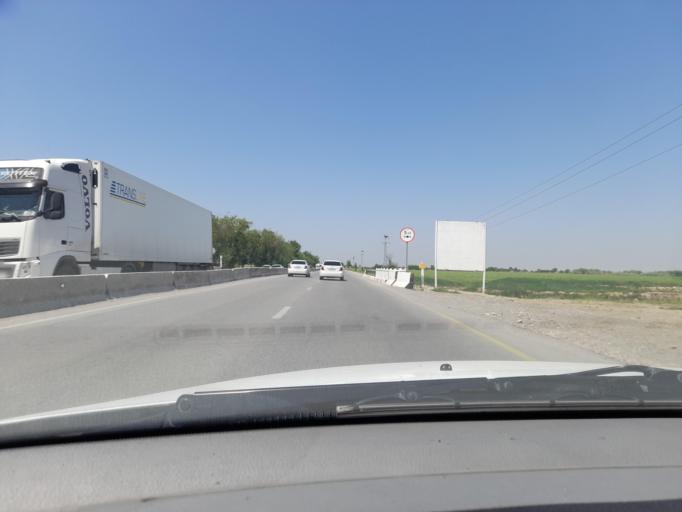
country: KZ
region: Ongtustik Qazaqstan
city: Myrzakent
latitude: 40.5545
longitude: 68.3947
